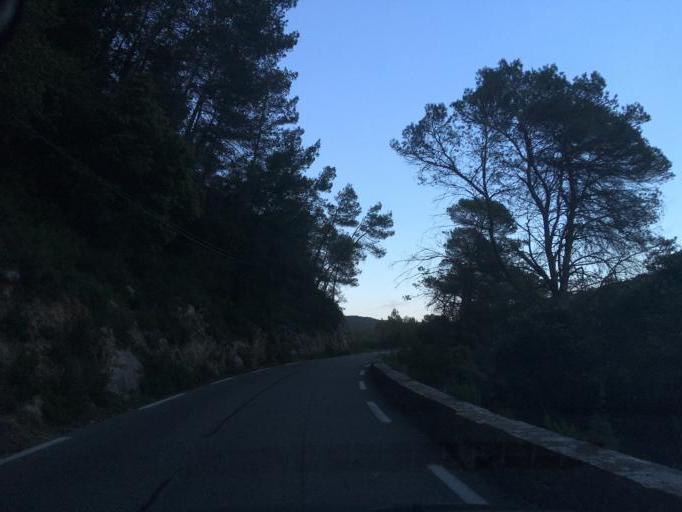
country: FR
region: Provence-Alpes-Cote d'Azur
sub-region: Departement du Var
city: Salernes
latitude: 43.5238
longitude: 6.2390
